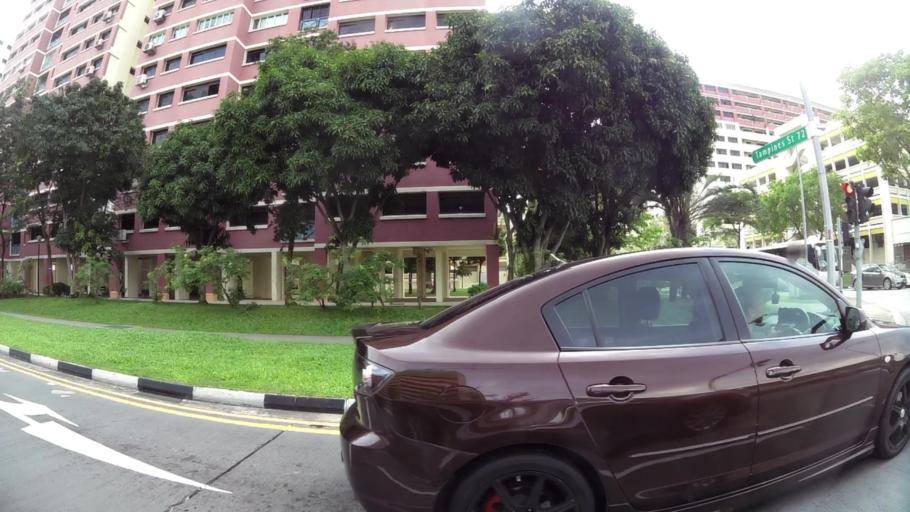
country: SG
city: Singapore
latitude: 1.3603
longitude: 103.9348
